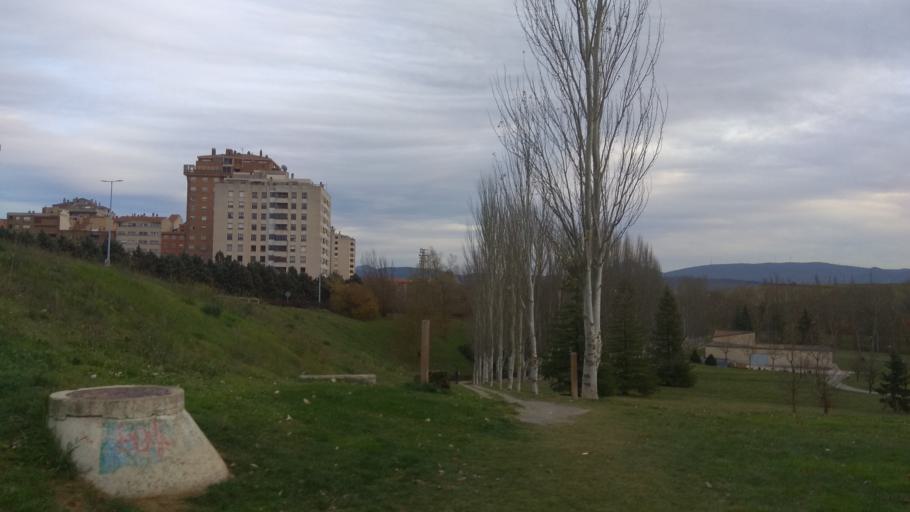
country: ES
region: Navarre
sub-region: Provincia de Navarra
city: Iturrama
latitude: 42.8012
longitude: -1.6500
